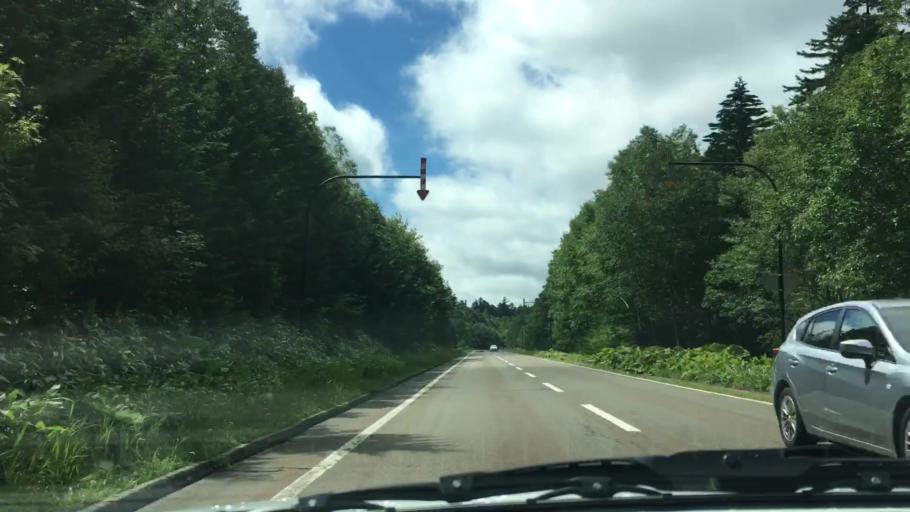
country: JP
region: Hokkaido
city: Kitami
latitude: 43.4321
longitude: 143.9936
